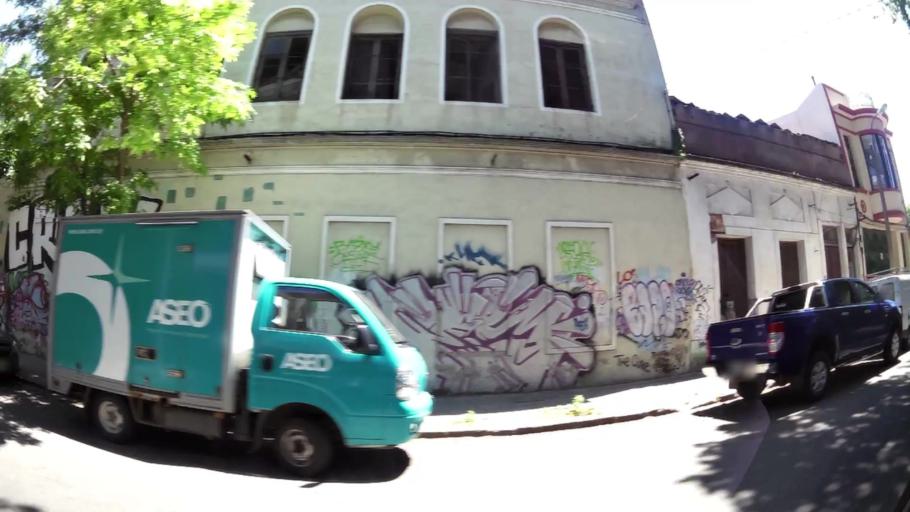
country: UY
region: Montevideo
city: Montevideo
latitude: -34.8974
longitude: -56.1849
